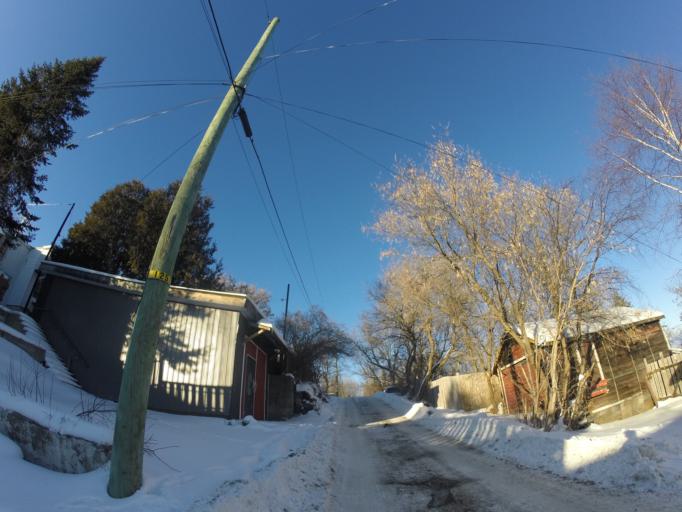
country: CA
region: Ontario
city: Greater Sudbury
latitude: 46.5033
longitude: -81.0000
